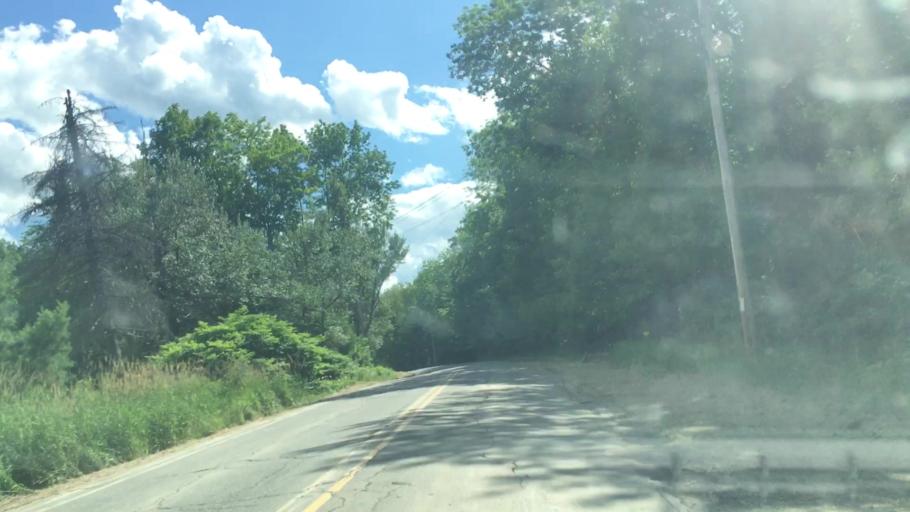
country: US
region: Maine
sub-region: Franklin County
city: Farmington
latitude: 44.7021
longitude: -70.1094
